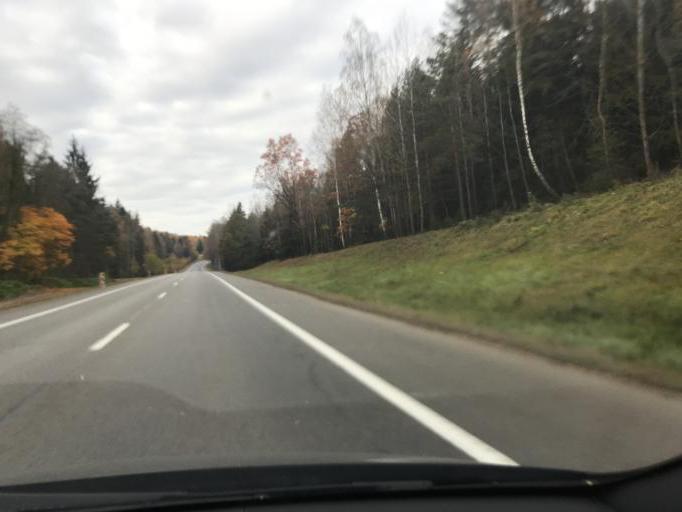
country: BY
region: Minsk
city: Slabada
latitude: 54.0362
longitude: 27.8333
